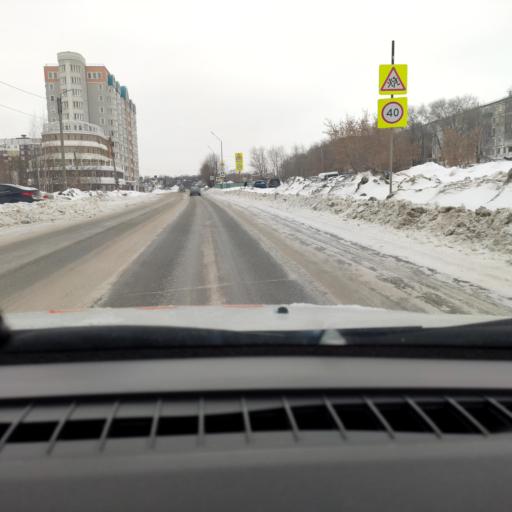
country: RU
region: Samara
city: Novokuybyshevsk
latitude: 53.0906
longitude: 49.9761
